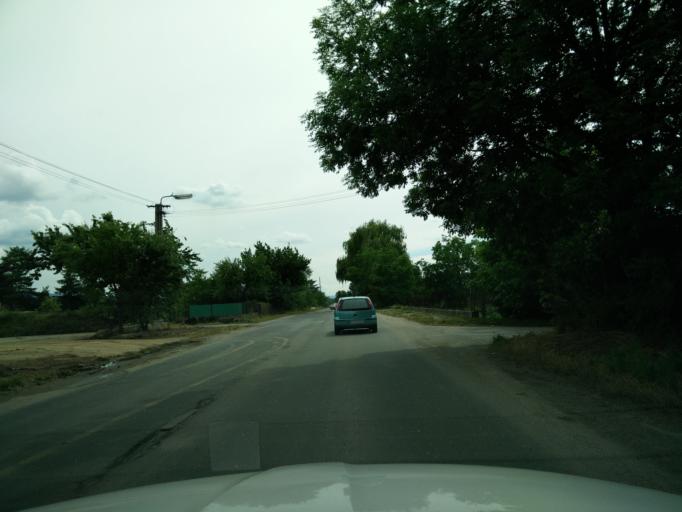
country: SK
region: Nitriansky
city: Bojnice
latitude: 48.7439
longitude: 18.5779
